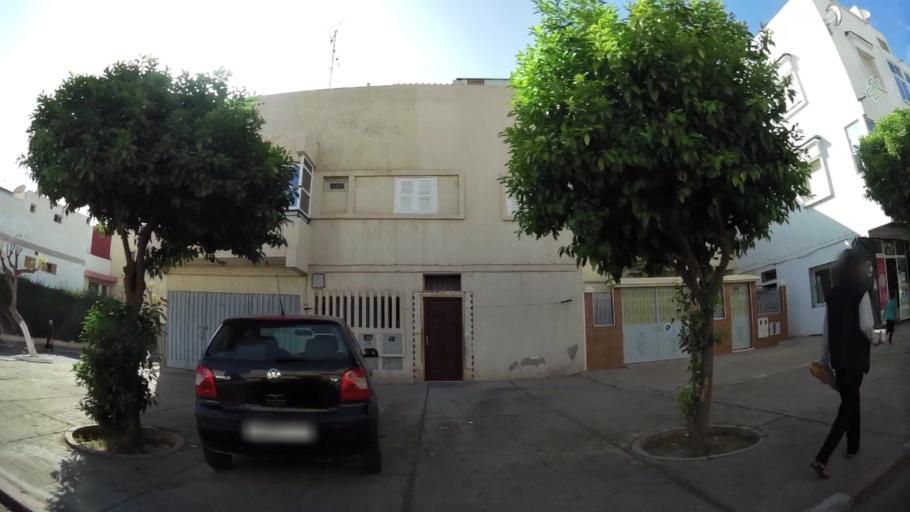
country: MA
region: Souss-Massa-Draa
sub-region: Agadir-Ida-ou-Tnan
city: Agadir
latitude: 30.4335
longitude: -9.5787
